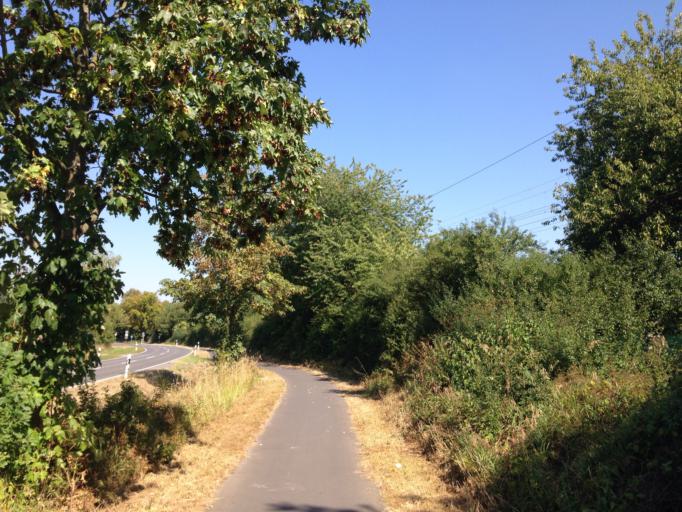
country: DE
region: Hesse
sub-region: Regierungsbezirk Giessen
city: Giessen
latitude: 50.6155
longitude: 8.6849
